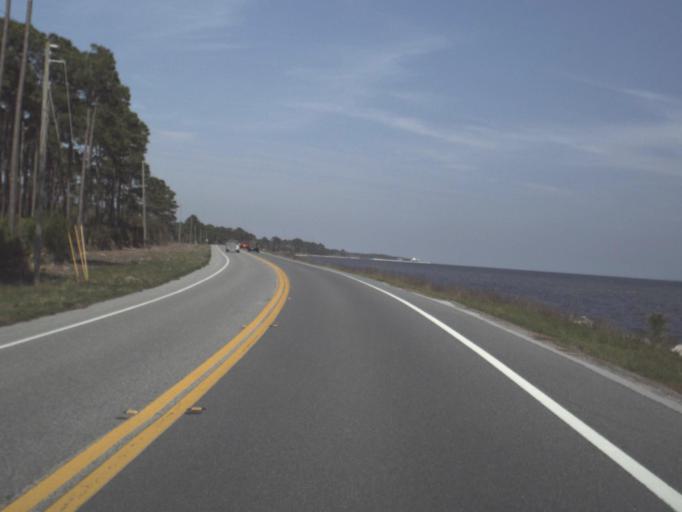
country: US
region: Florida
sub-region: Franklin County
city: Eastpoint
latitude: 29.7693
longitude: -84.7983
